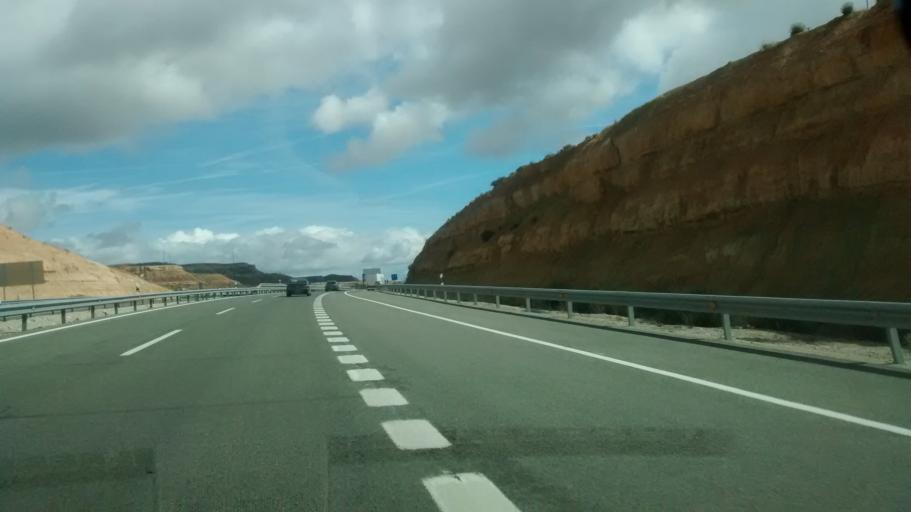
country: ES
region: Castille and Leon
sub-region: Provincia de Soria
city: Arcos de Jalon
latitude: 41.2197
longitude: -2.2848
